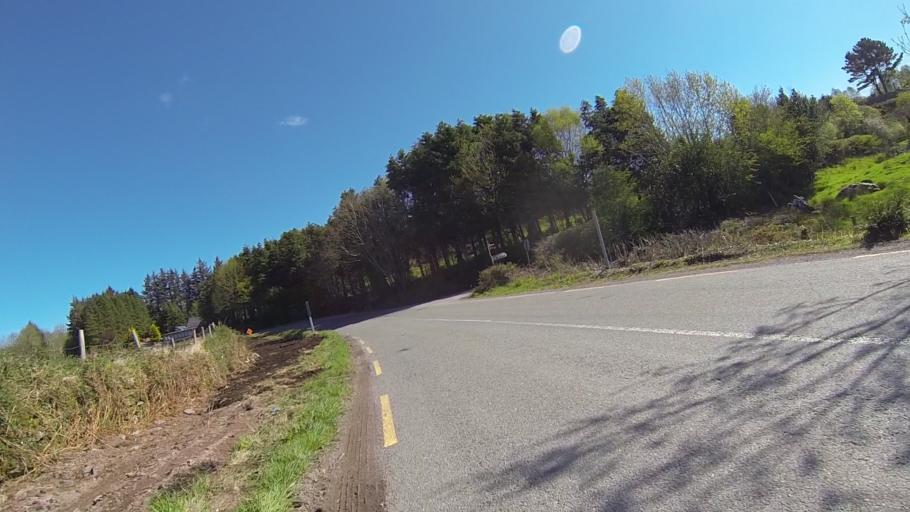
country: IE
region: Munster
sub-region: Ciarrai
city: Kenmare
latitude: 51.8527
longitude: -9.6276
